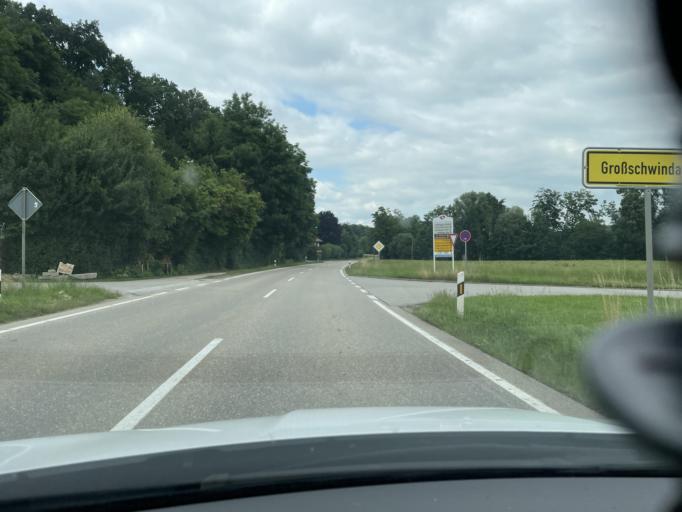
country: DE
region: Bavaria
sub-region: Upper Bavaria
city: Sankt Wolfgang
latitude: 48.2322
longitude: 12.1389
